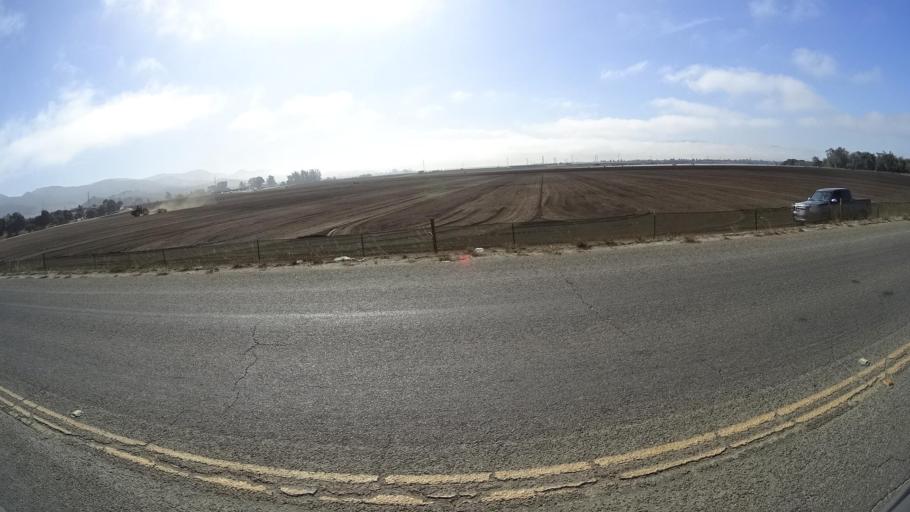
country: US
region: California
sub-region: Monterey County
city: Salinas
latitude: 36.7326
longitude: -121.6097
